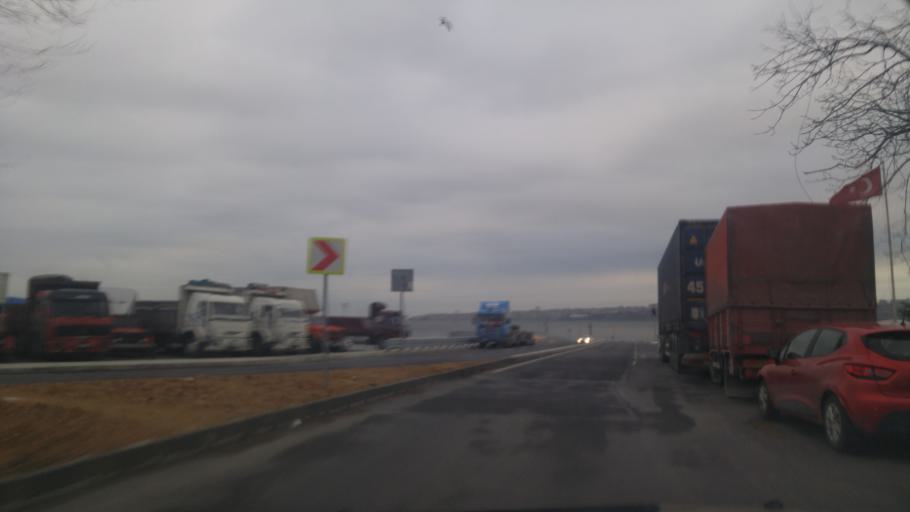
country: TR
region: Istanbul
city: Mahmutbey
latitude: 41.0131
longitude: 28.7686
